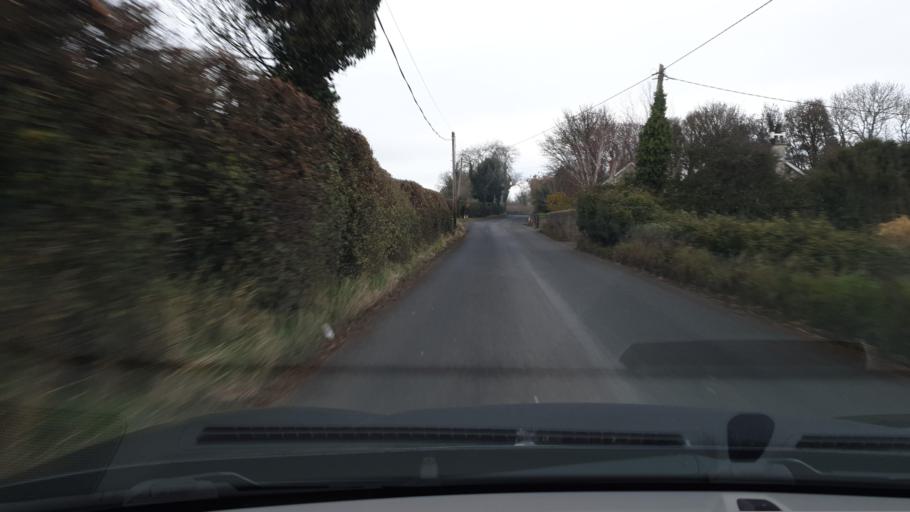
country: IE
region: Leinster
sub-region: An Mhi
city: Ashbourne
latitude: 53.5310
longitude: -6.4072
